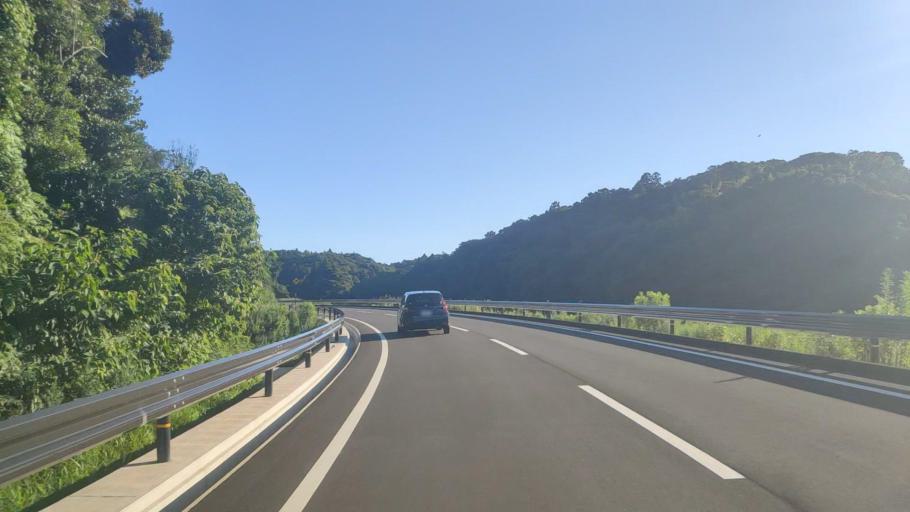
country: JP
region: Mie
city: Toba
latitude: 34.3127
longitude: 136.8817
